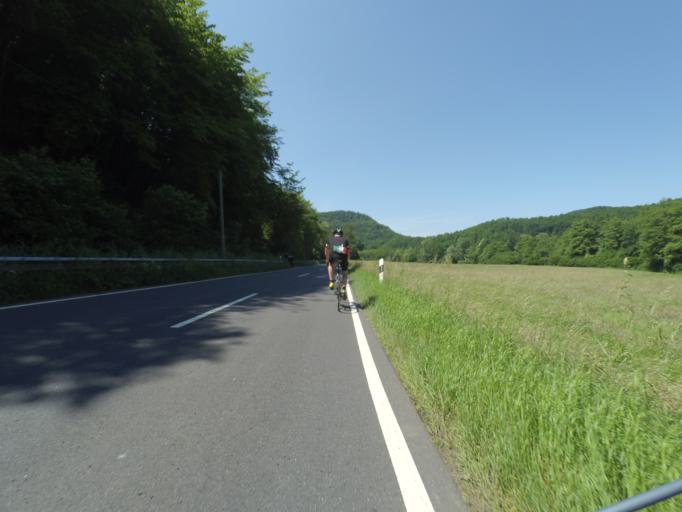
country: DE
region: Rheinland-Pfalz
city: Altstrimmig
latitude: 50.1216
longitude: 7.2856
